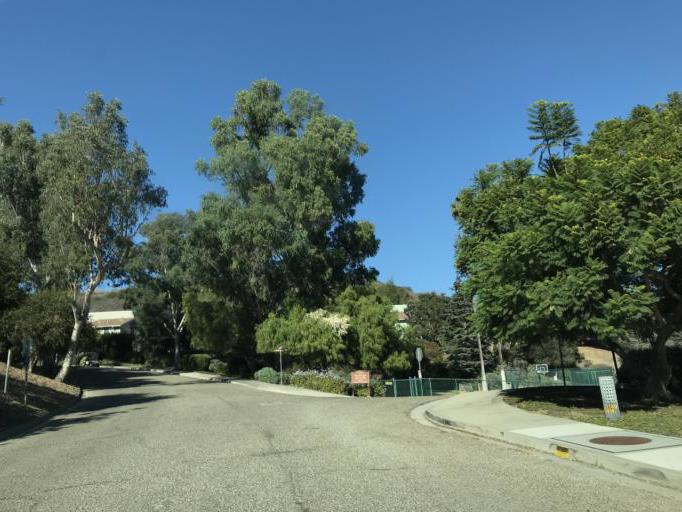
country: US
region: California
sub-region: Santa Barbara County
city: Goleta
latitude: 34.4467
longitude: -119.7794
